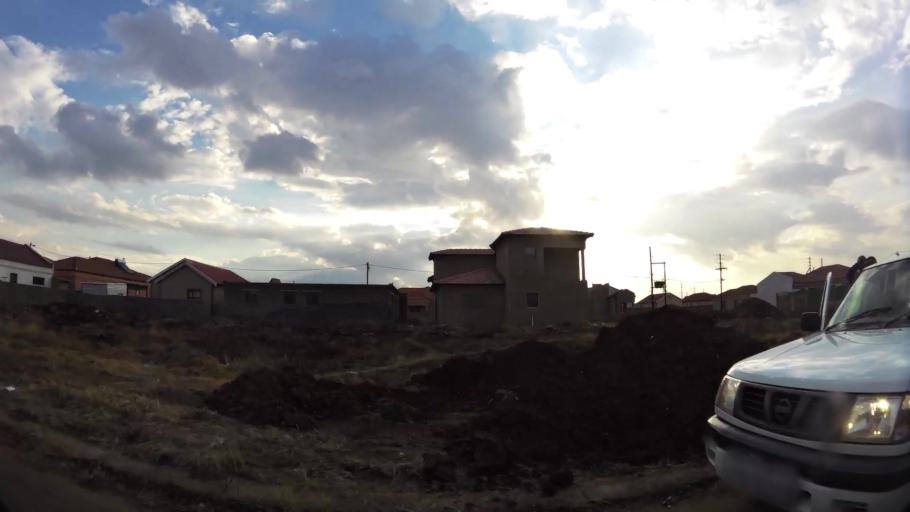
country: ZA
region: Gauteng
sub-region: Sedibeng District Municipality
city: Vanderbijlpark
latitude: -26.6116
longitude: 27.8144
